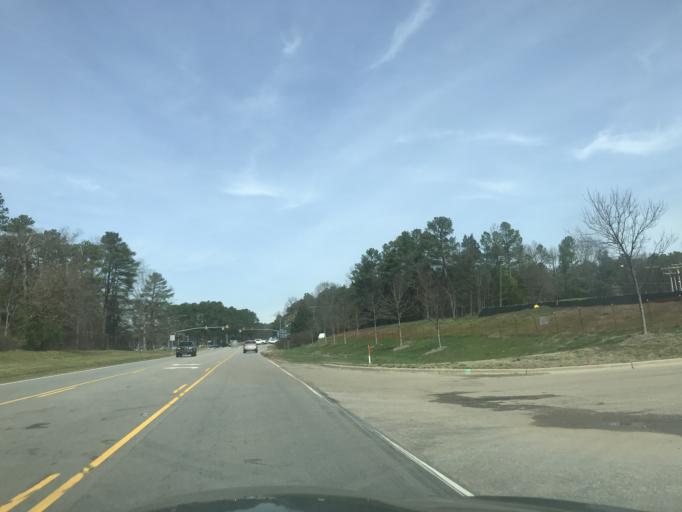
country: US
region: North Carolina
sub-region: Wake County
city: Morrisville
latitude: 35.8971
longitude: -78.8798
